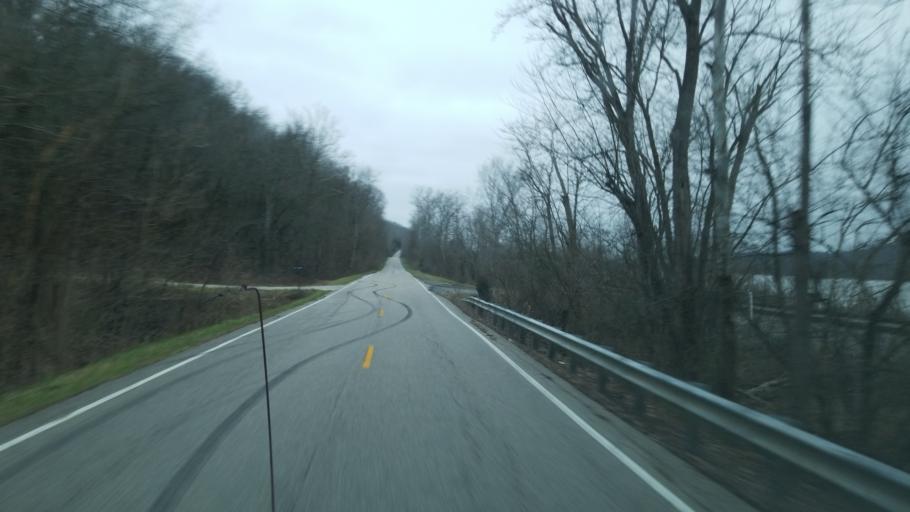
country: US
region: Kentucky
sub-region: Bracken County
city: Augusta
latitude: 38.7666
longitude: -84.0398
